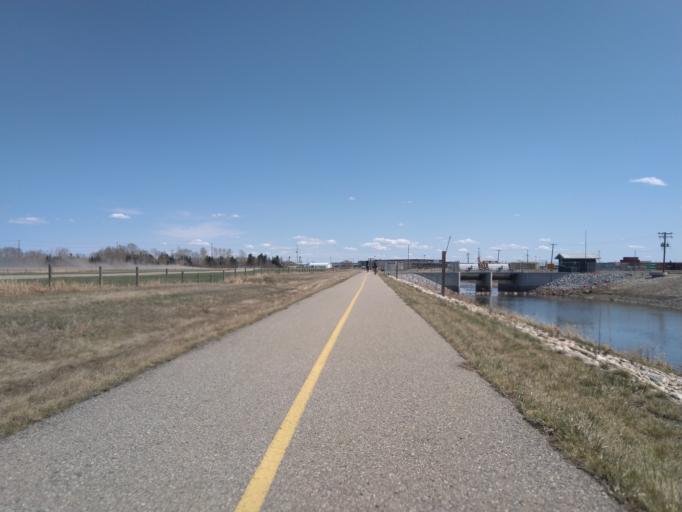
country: CA
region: Alberta
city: Chestermere
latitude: 50.9728
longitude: -113.9173
